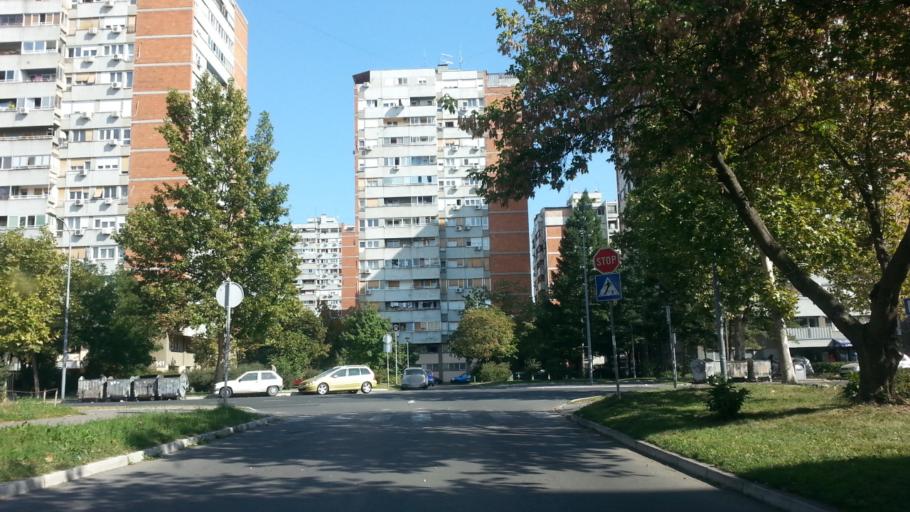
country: RS
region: Central Serbia
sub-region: Belgrade
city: Novi Beograd
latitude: 44.8013
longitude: 20.3884
